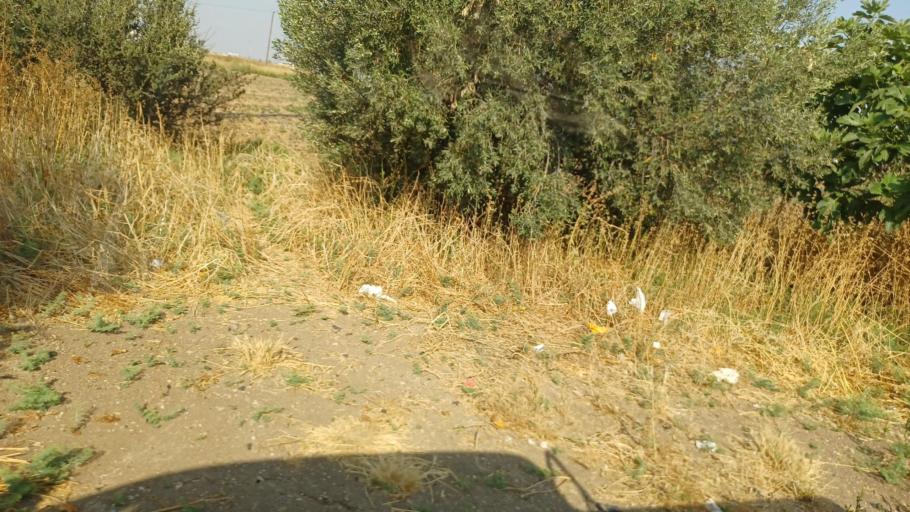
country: CY
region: Larnaka
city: Meneou
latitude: 34.8729
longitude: 33.6035
